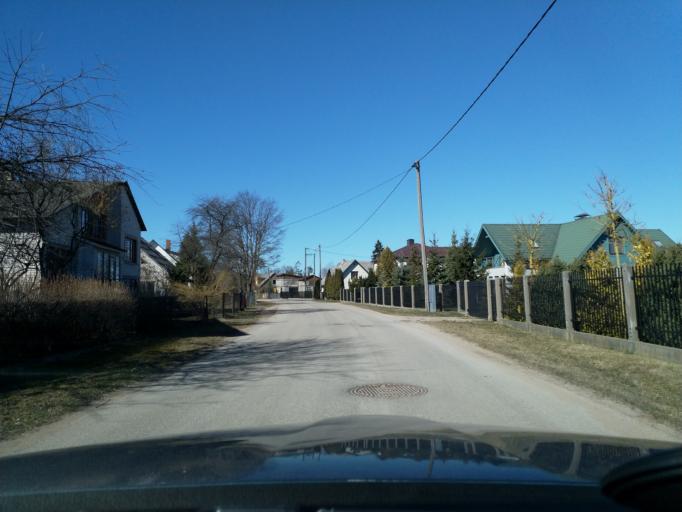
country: LV
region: Kuldigas Rajons
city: Kuldiga
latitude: 56.9659
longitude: 21.9972
